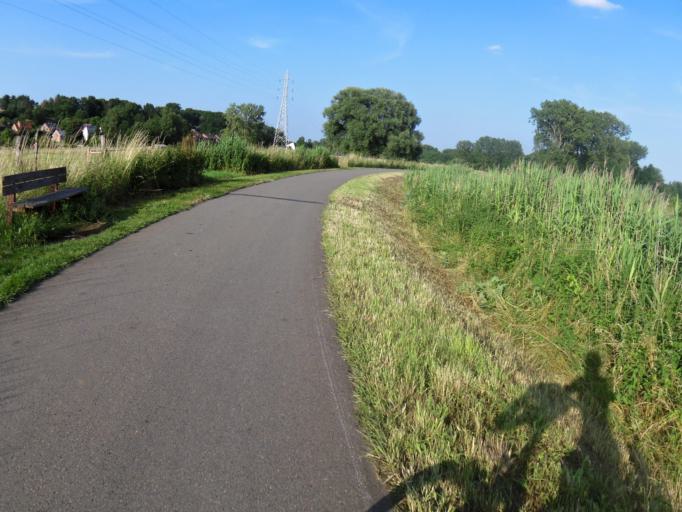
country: BE
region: Flanders
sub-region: Provincie Vlaams-Brabant
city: Aarschot
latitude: 50.9862
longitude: 4.8517
